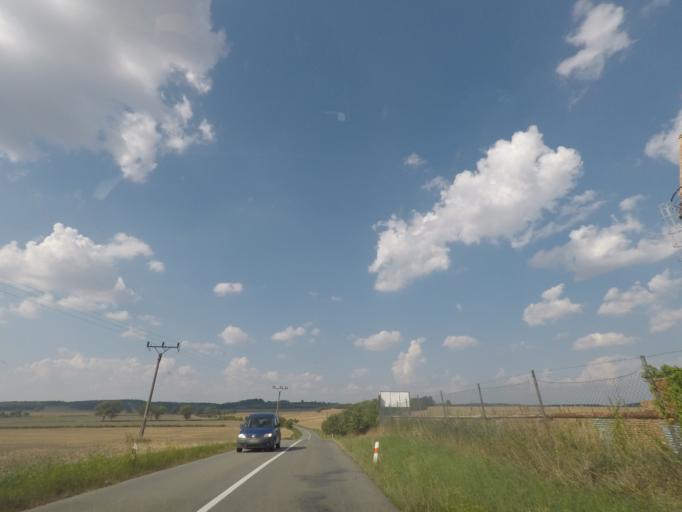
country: CZ
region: Kralovehradecky
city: Trebechovice pod Orebem
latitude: 50.2068
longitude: 15.9893
